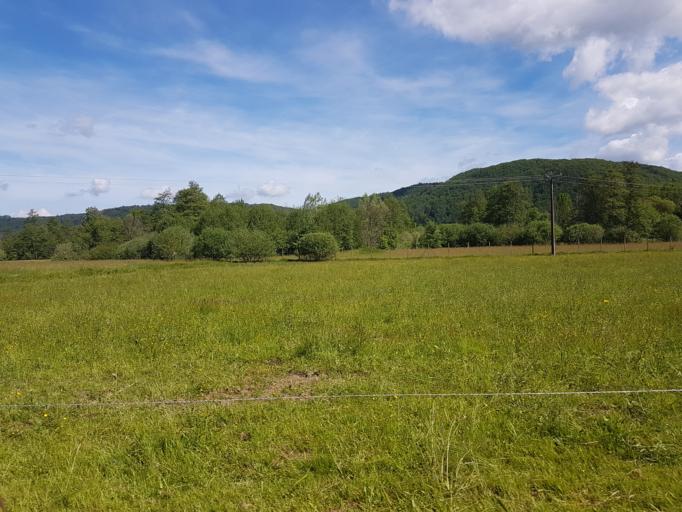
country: FR
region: Franche-Comte
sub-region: Departement de la Haute-Saone
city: Melisey
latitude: 47.8237
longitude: 6.5449
